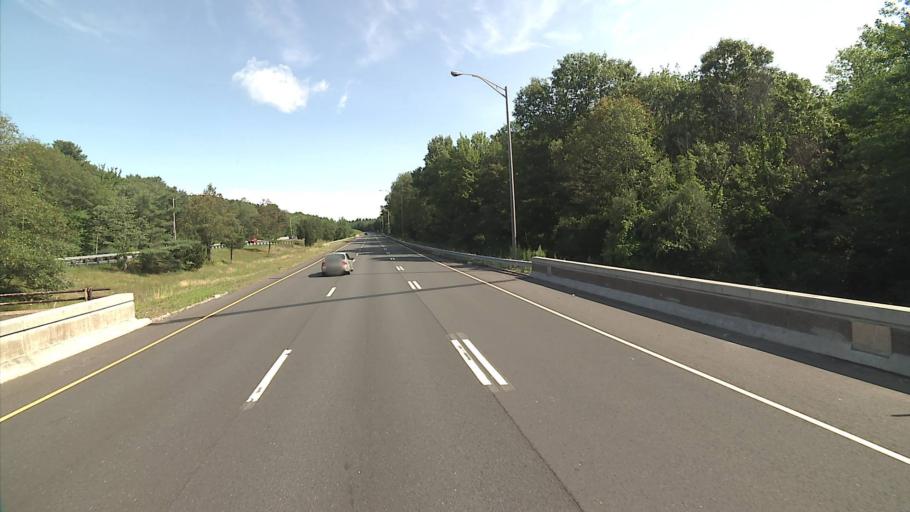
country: US
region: Connecticut
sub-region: Hartford County
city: Glastonbury Center
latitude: 41.6817
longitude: -72.5411
